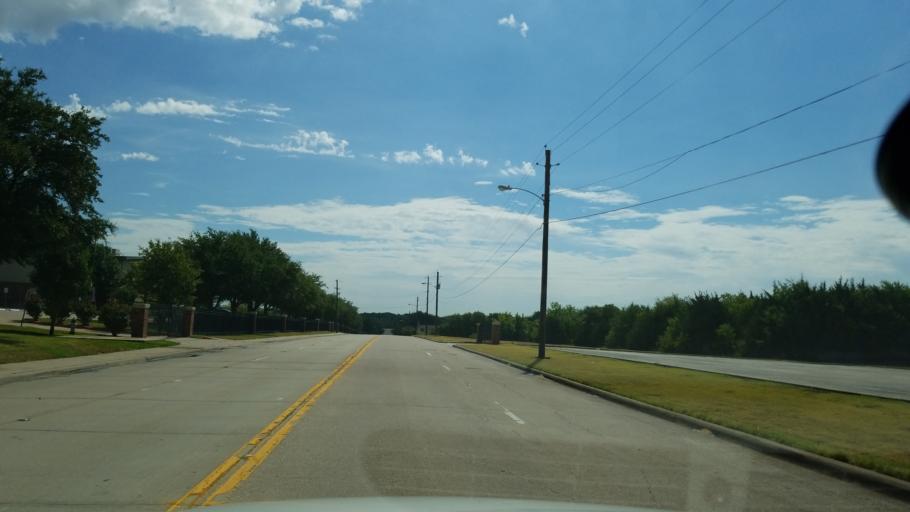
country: US
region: Texas
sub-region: Dallas County
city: Duncanville
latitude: 32.6549
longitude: -96.8565
